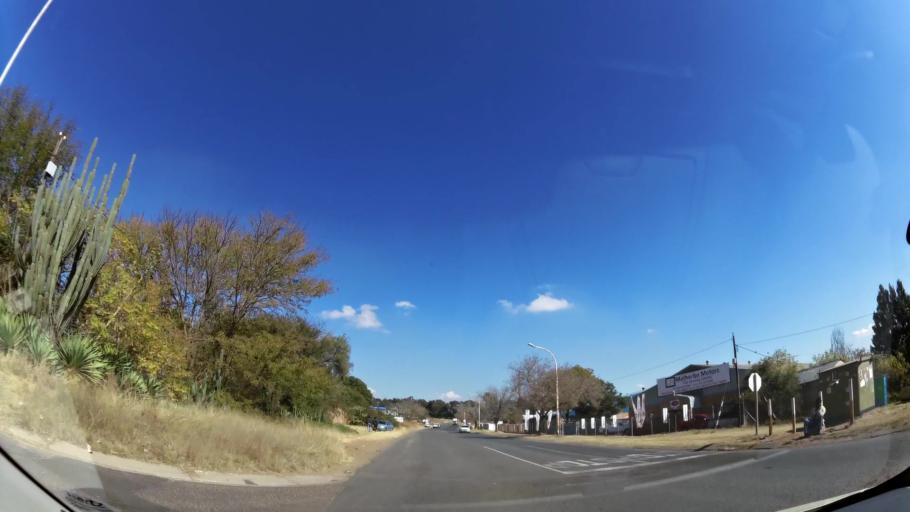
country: ZA
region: Mpumalanga
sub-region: Nkangala District Municipality
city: Witbank
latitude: -25.8584
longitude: 29.2371
